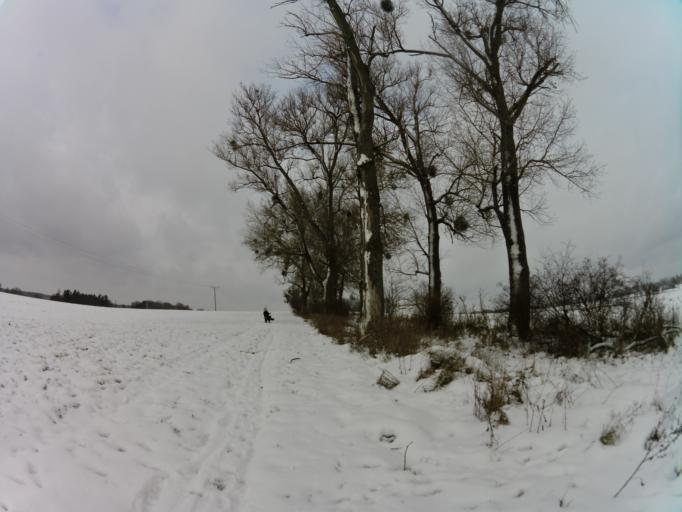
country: PL
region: West Pomeranian Voivodeship
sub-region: Powiat choszczenski
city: Recz
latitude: 53.3043
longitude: 15.5569
